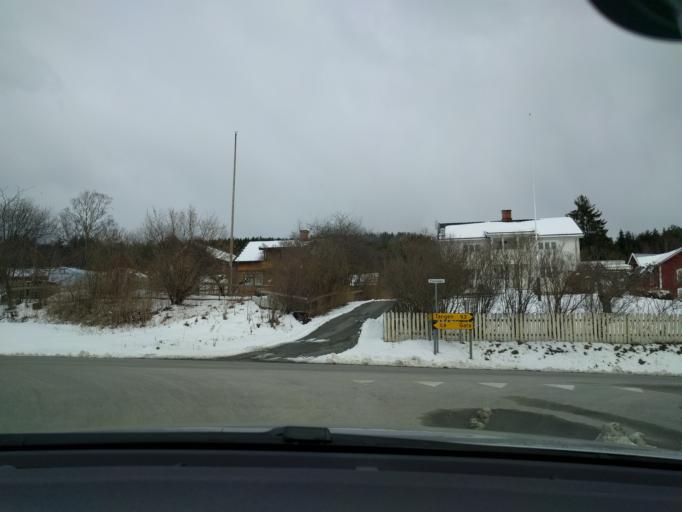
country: NO
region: Hedmark
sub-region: Loten
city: Loten
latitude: 60.6785
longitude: 11.3465
